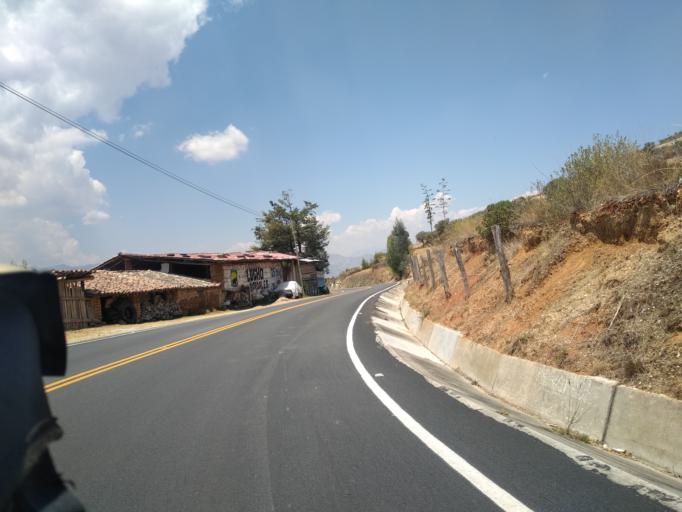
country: PE
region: Cajamarca
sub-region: San Marcos
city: San Marcos
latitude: -7.2754
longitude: -78.2454
